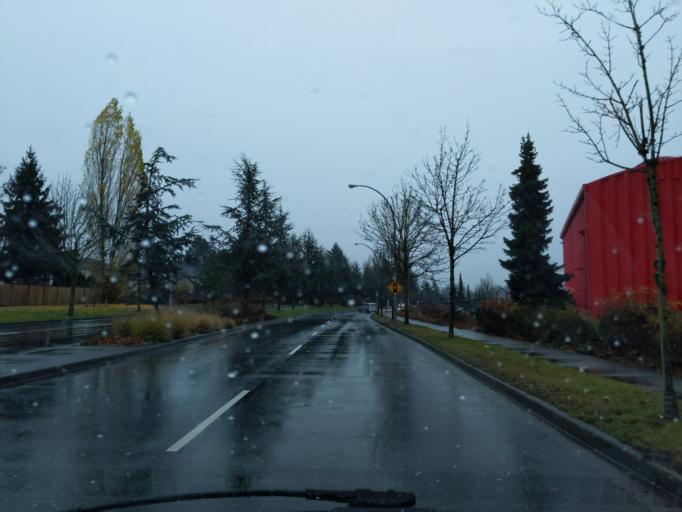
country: CA
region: British Columbia
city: Walnut Grove
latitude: 49.1702
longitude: -122.6630
